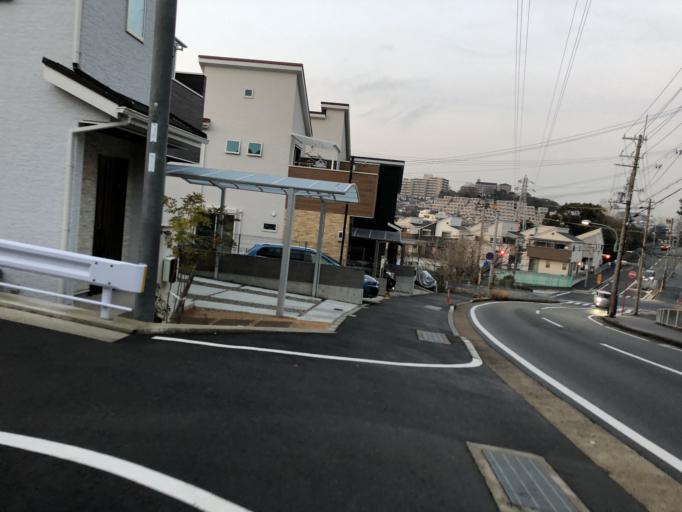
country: JP
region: Hyogo
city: Akashi
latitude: 34.6525
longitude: 135.0200
